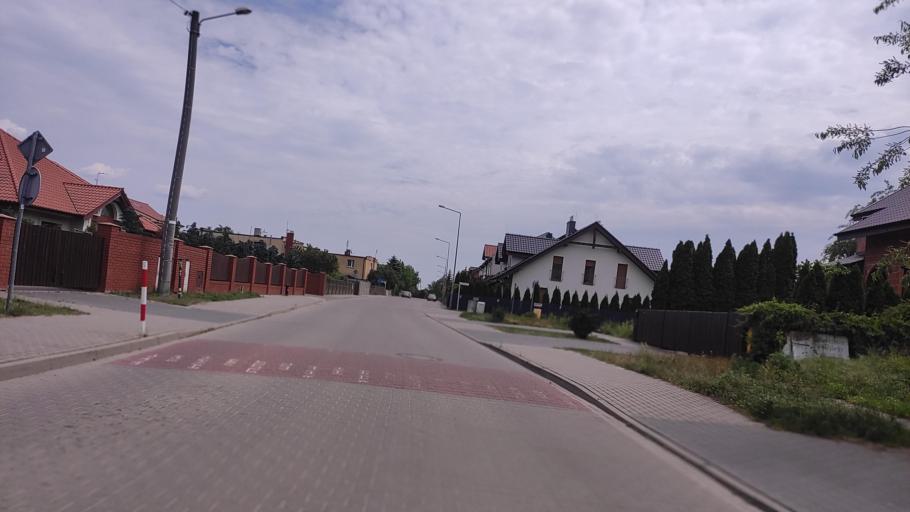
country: PL
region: Greater Poland Voivodeship
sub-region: Powiat poznanski
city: Swarzedz
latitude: 52.3954
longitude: 17.0734
